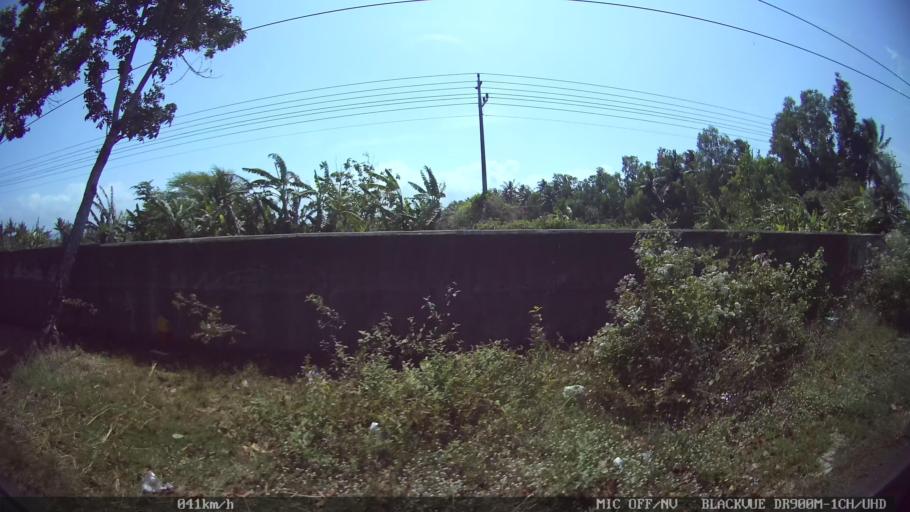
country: ID
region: Daerah Istimewa Yogyakarta
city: Srandakan
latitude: -7.9323
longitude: 110.1432
